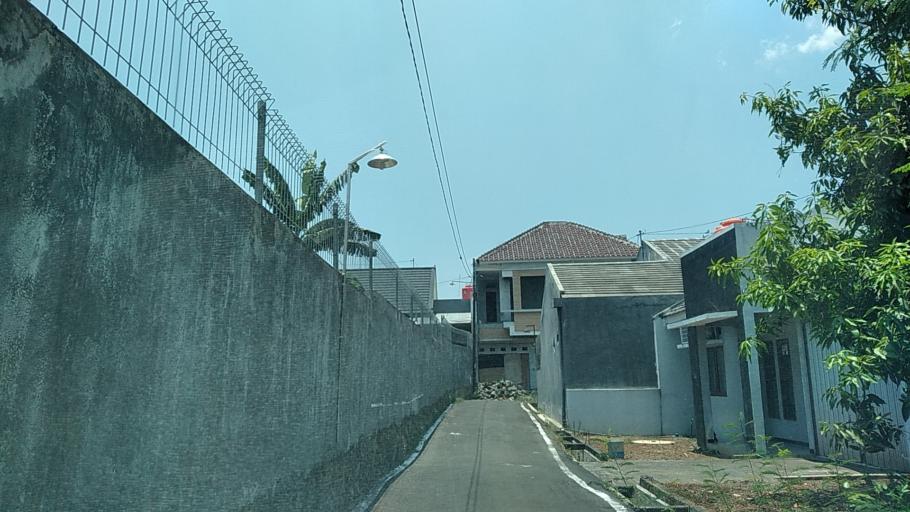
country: ID
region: Central Java
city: Ungaran
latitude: -7.0775
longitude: 110.4243
